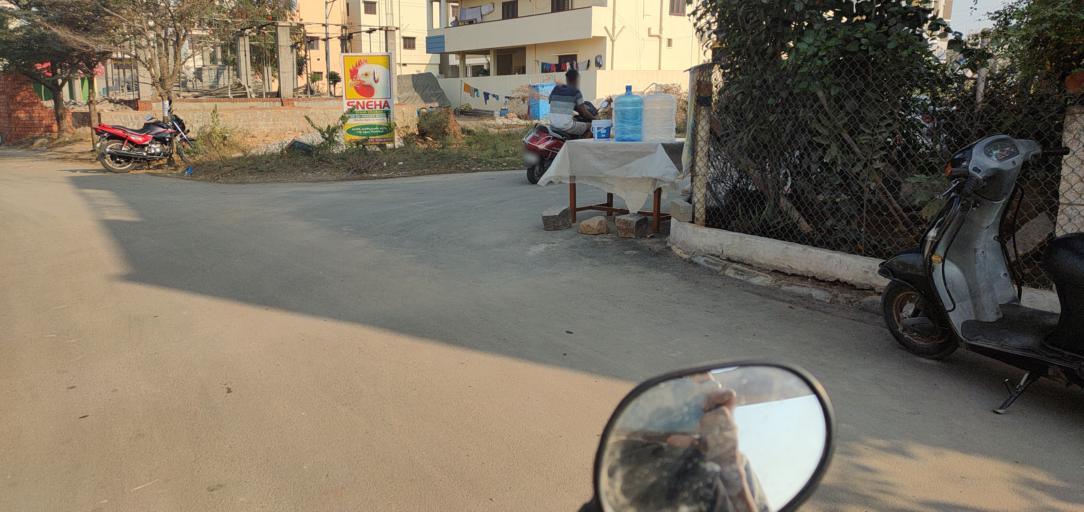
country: IN
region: Telangana
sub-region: Rangareddi
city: Lal Bahadur Nagar
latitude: 17.3320
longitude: 78.6143
